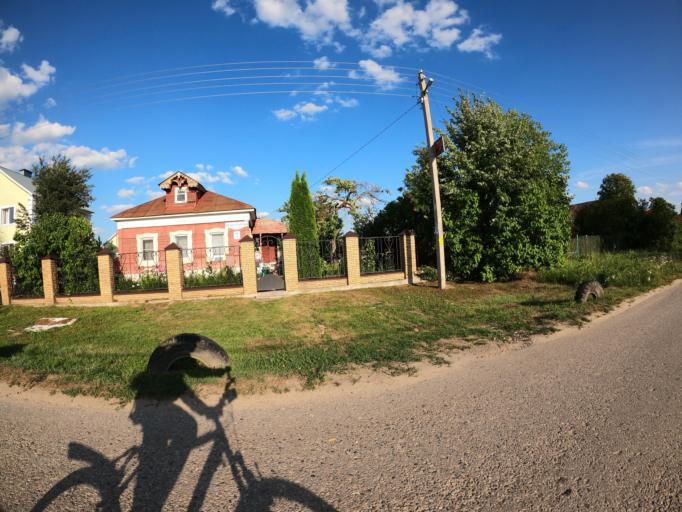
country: RU
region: Moskovskaya
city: Raduzhnyy
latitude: 55.1479
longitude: 38.7356
